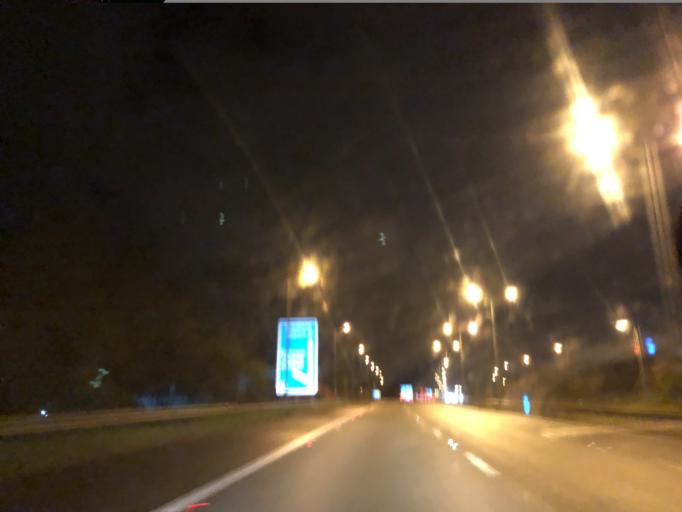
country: GB
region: England
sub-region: Kirklees
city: Cleckheaton
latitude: 53.7520
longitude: -1.7407
